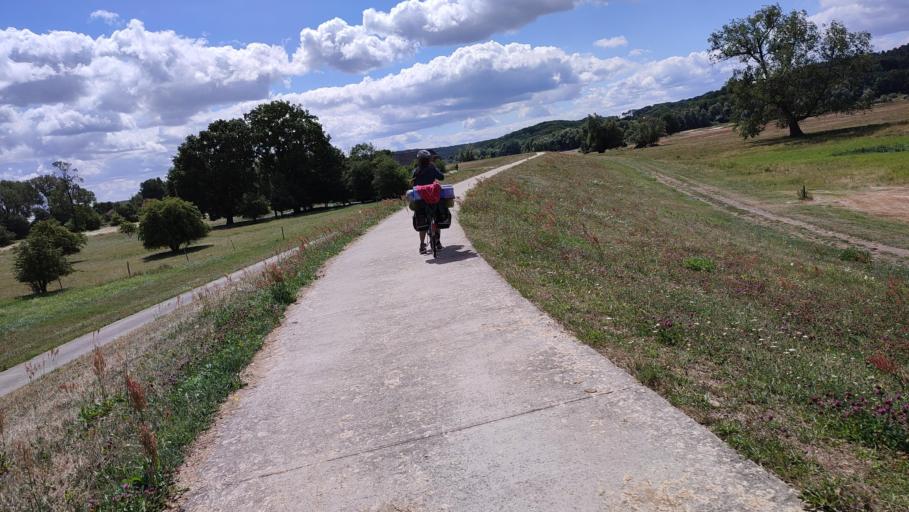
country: DE
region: Lower Saxony
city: Hitzacker
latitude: 53.2002
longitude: 10.9804
